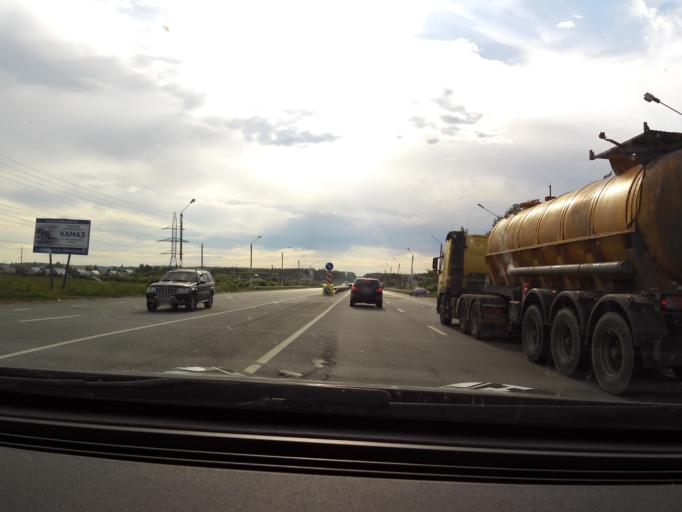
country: RU
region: Vladimir
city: Novovyazniki
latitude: 56.2189
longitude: 42.1931
